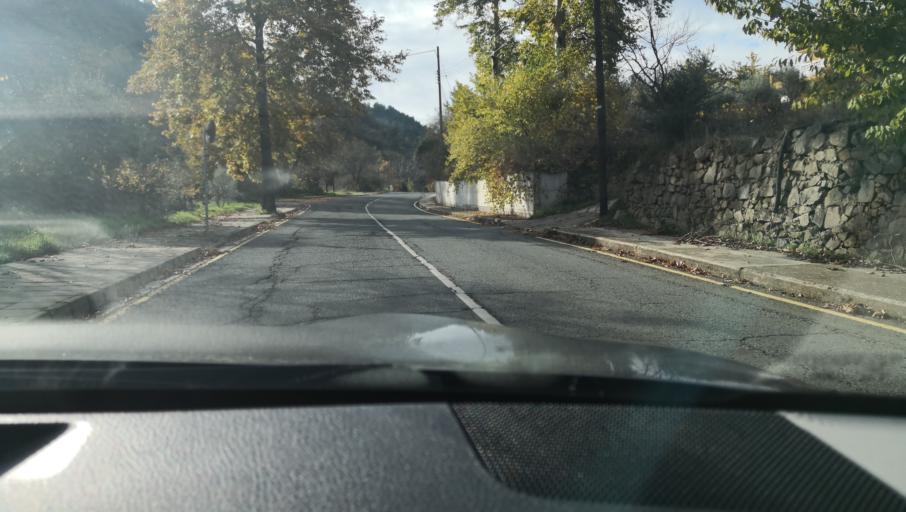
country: CY
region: Lefkosia
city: Lefka
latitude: 35.0351
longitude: 32.7322
